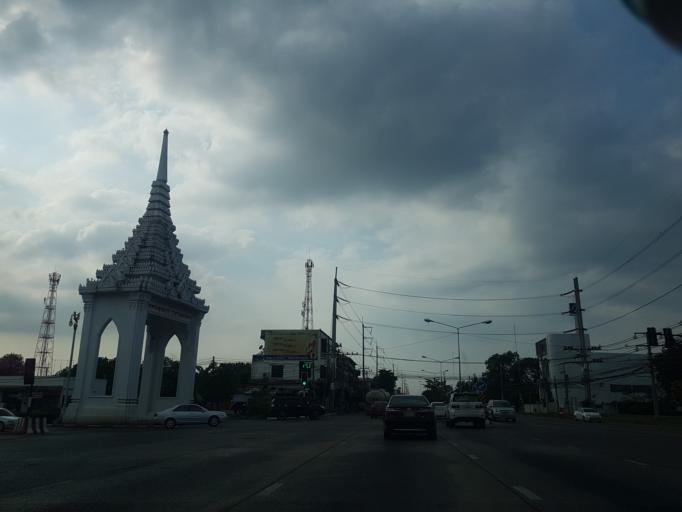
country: TH
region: Sara Buri
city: Phra Phutthabat
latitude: 14.7268
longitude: 100.7942
